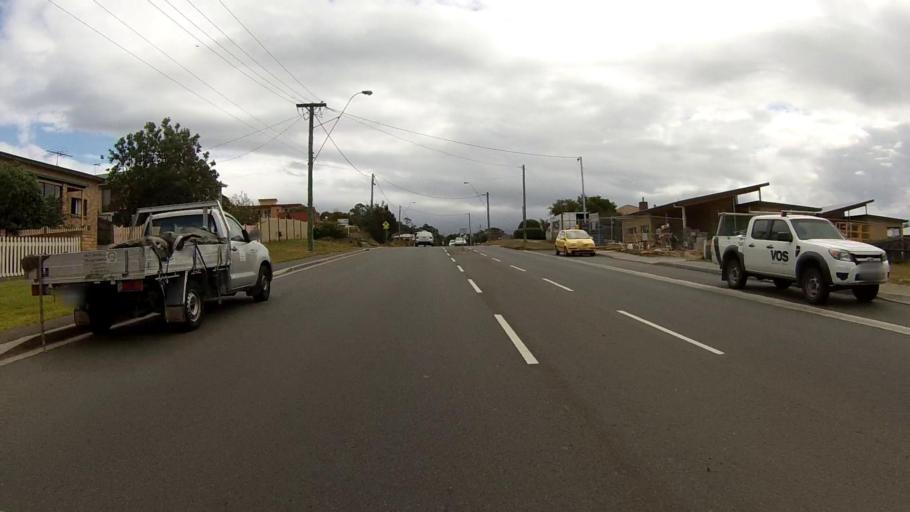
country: AU
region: Tasmania
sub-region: Clarence
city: Warrane
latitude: -42.8576
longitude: 147.3909
